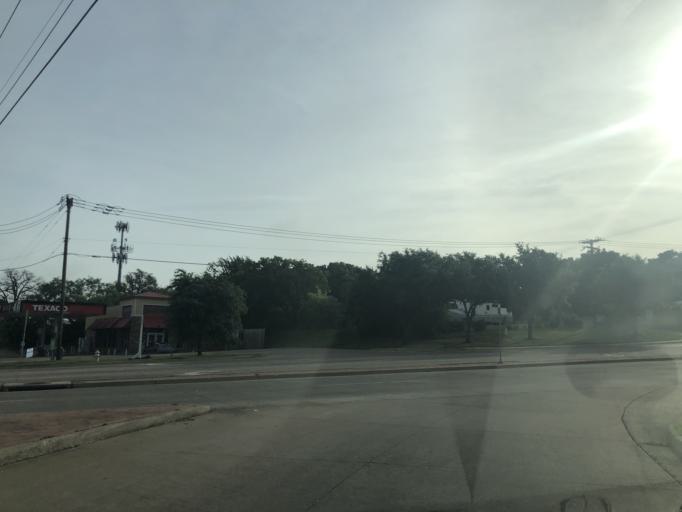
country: US
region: Texas
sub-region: Dallas County
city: Irving
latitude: 32.8048
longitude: -96.9943
